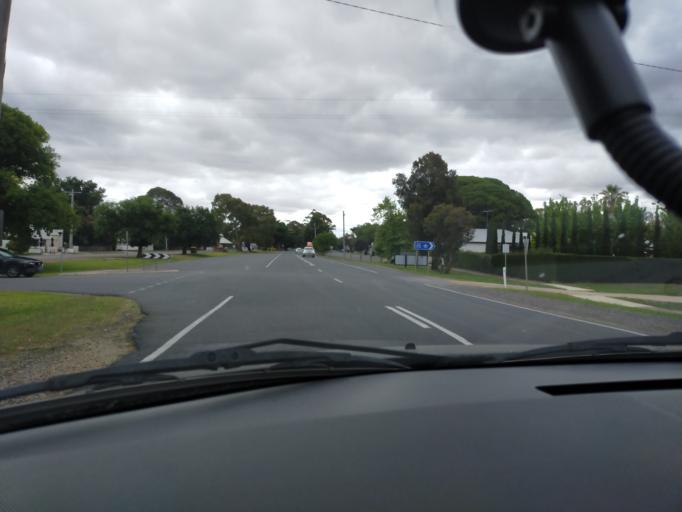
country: AU
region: Victoria
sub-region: Greater Geelong
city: Wandana Heights
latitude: -38.1002
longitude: 144.0611
